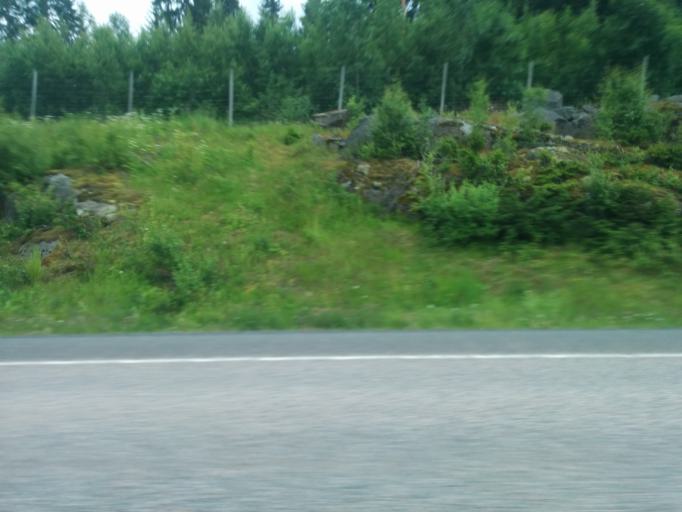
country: FI
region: Pirkanmaa
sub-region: Tampere
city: Orivesi
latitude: 61.7090
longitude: 24.4785
